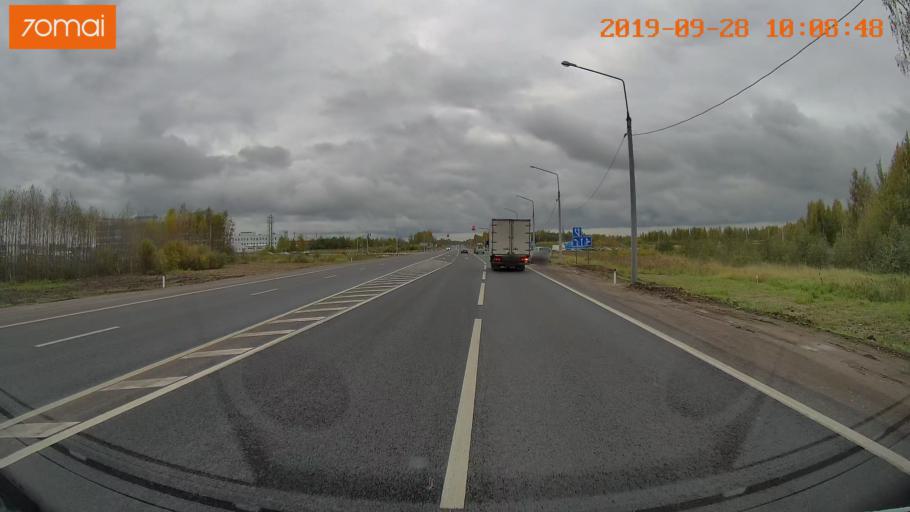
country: RU
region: Jaroslavl
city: Yaroslavl
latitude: 57.5514
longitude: 39.8875
